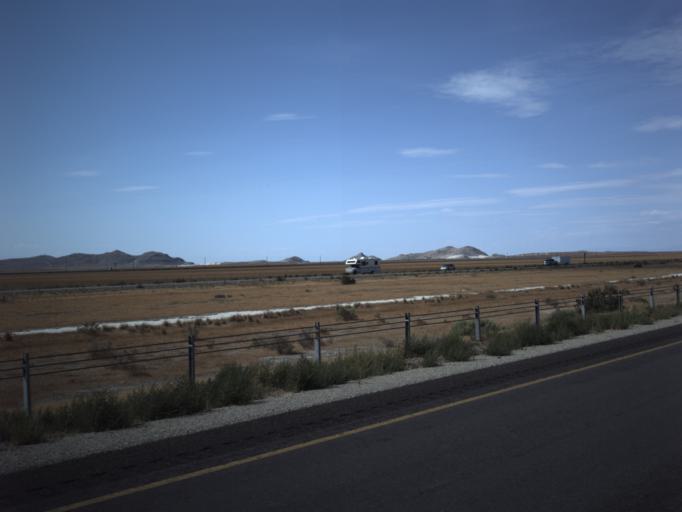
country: US
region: Utah
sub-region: Tooele County
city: Grantsville
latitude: 40.7271
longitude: -113.2342
